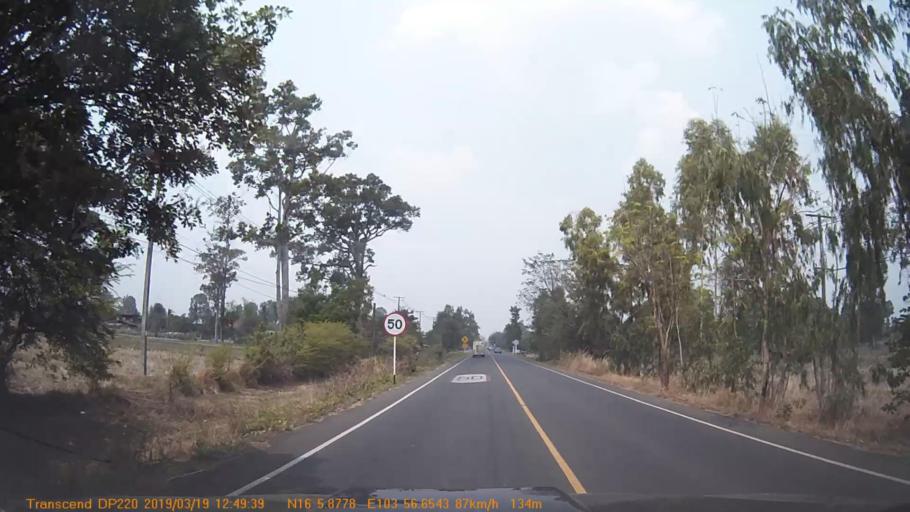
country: TH
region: Roi Et
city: Selaphum
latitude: 16.0984
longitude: 103.9443
